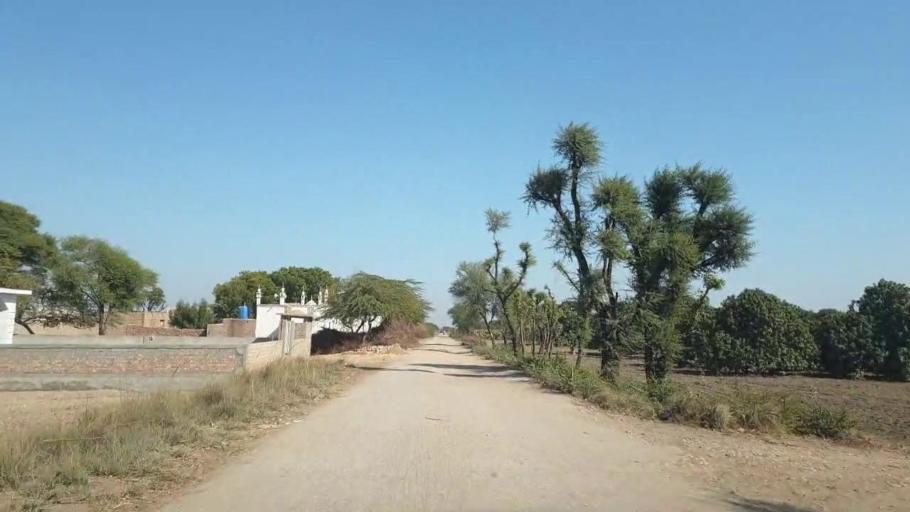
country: PK
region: Sindh
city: Tando Adam
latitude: 25.6625
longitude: 68.6885
